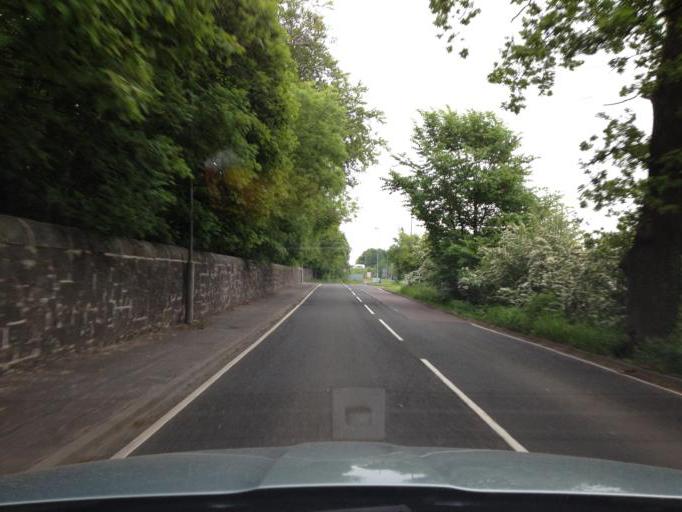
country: GB
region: Scotland
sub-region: West Dunbartonshire
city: Old Kilpatrick
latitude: 55.9140
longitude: -4.4775
